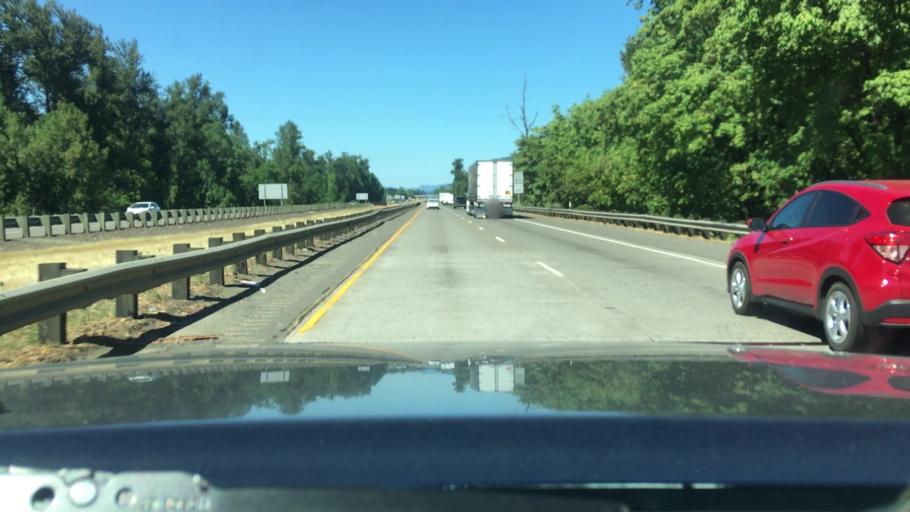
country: US
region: Oregon
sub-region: Lane County
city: Cottage Grove
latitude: 43.8139
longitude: -123.0384
